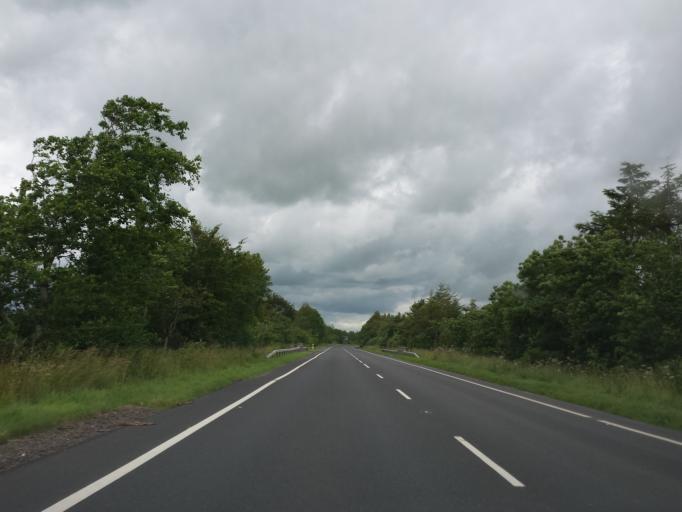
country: GB
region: Scotland
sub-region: Dumfries and Galloway
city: Castle Douglas
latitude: 54.9411
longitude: -3.9461
